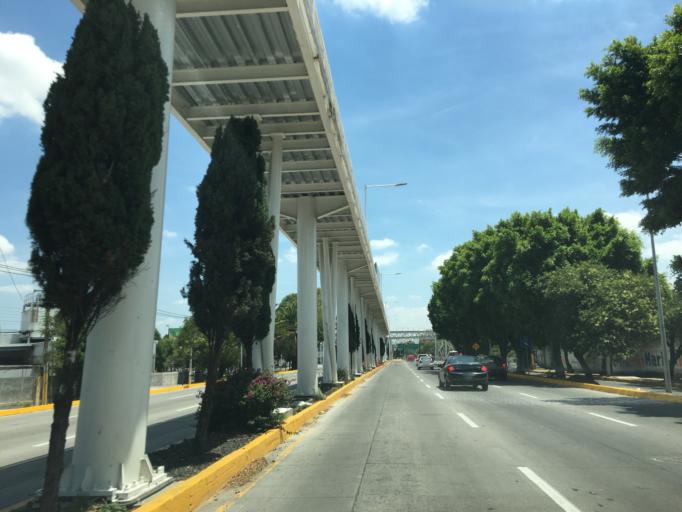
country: MX
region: Puebla
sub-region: Cuautlancingo
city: Sanctorum
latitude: 19.0891
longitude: -98.2293
